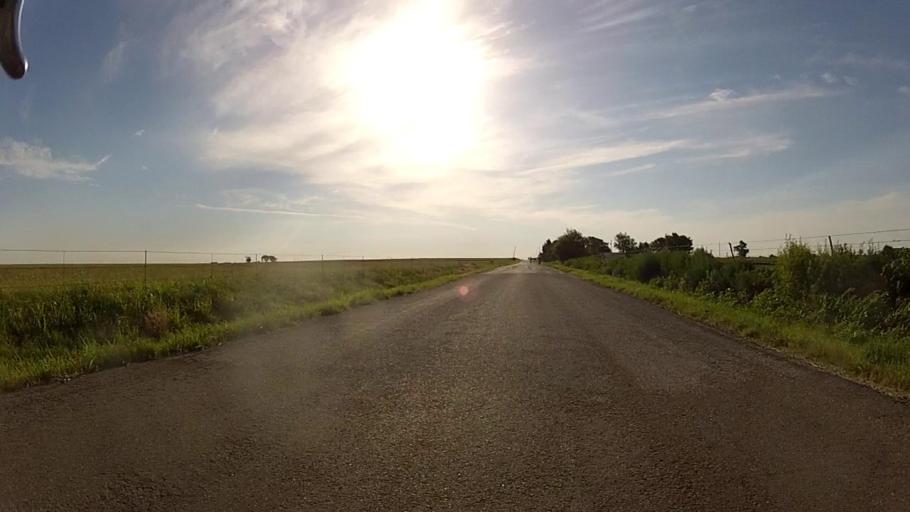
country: US
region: Kansas
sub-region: Cowley County
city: Arkansas City
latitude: 37.0485
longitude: -96.8345
